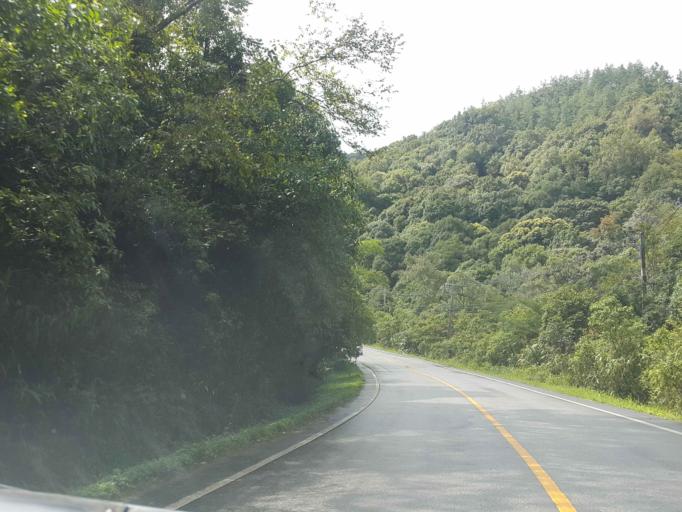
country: TH
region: Chiang Mai
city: Mae Chaem
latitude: 18.5107
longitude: 98.5096
